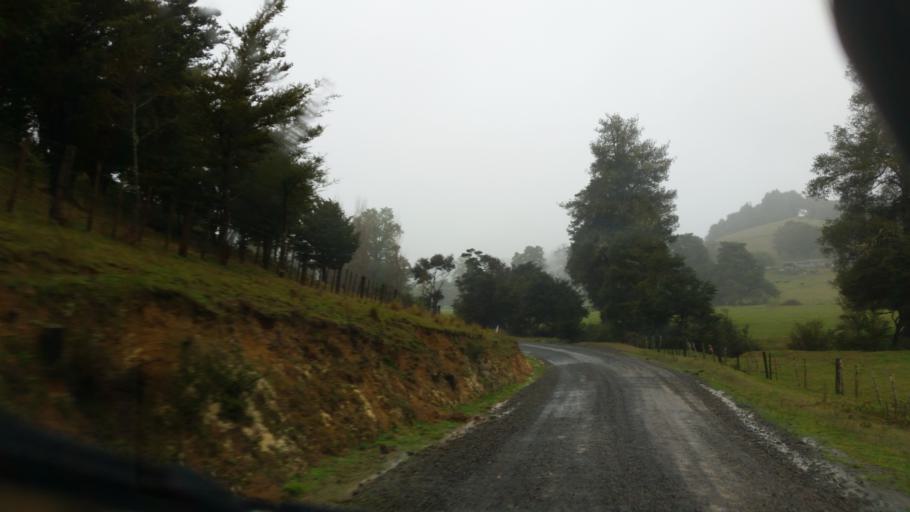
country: NZ
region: Northland
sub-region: Whangarei
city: Ngunguru
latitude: -35.4978
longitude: 174.4283
